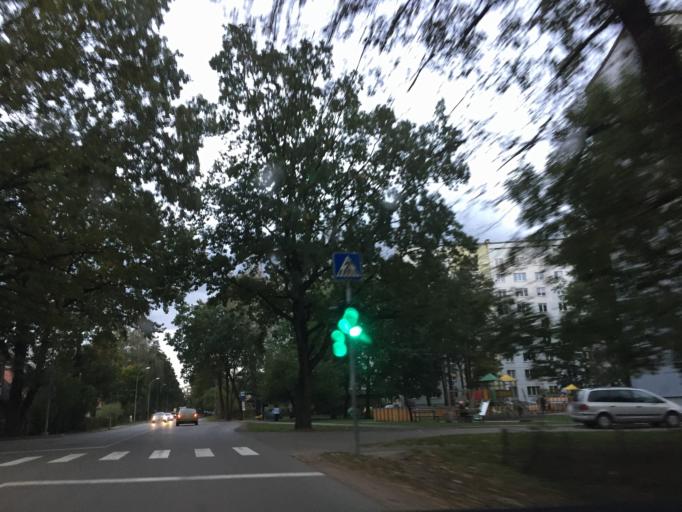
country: LV
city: Tireli
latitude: 56.9529
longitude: 23.6090
